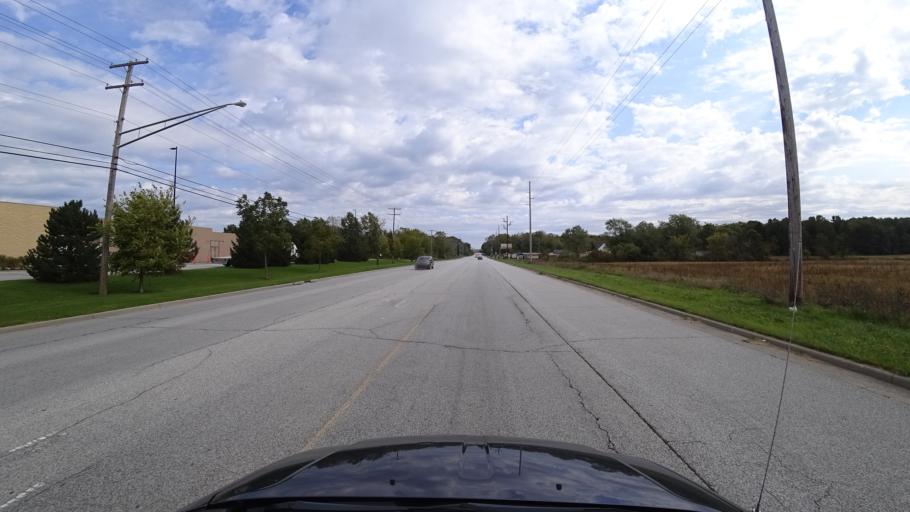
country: US
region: Indiana
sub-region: LaPorte County
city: Michigan City
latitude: 41.6658
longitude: -86.8887
